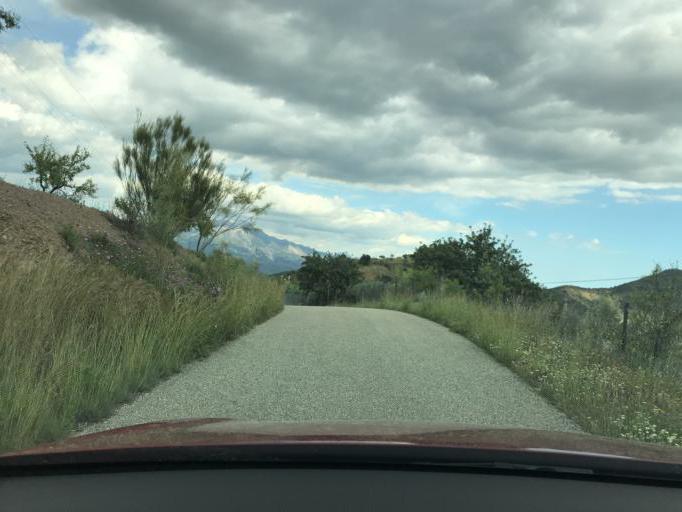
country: ES
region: Andalusia
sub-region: Provincia de Malaga
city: Comares
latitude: 36.8701
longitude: -4.2725
